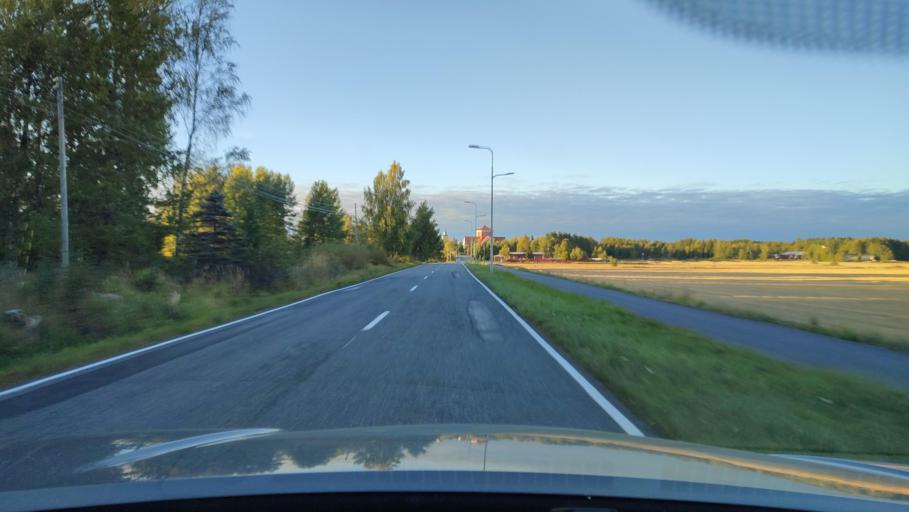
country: FI
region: Ostrobothnia
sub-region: Sydosterbotten
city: Kristinestad
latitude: 62.2397
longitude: 21.5209
